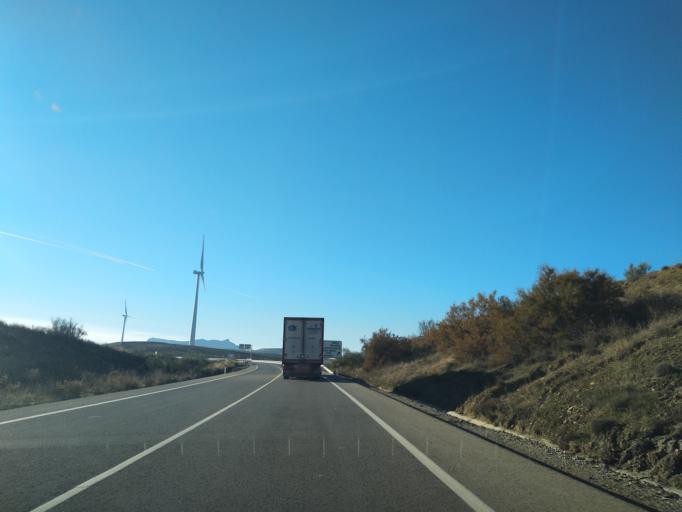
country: ES
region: Andalusia
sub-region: Provincia de Malaga
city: Teba
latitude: 36.9439
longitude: -4.8669
